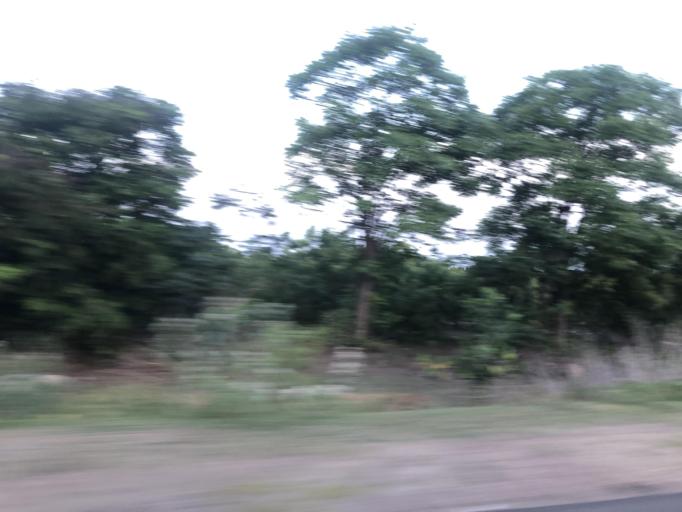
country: IN
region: Tamil Nadu
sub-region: Kancheepuram
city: Mamallapuram
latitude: 12.7612
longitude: 80.2448
